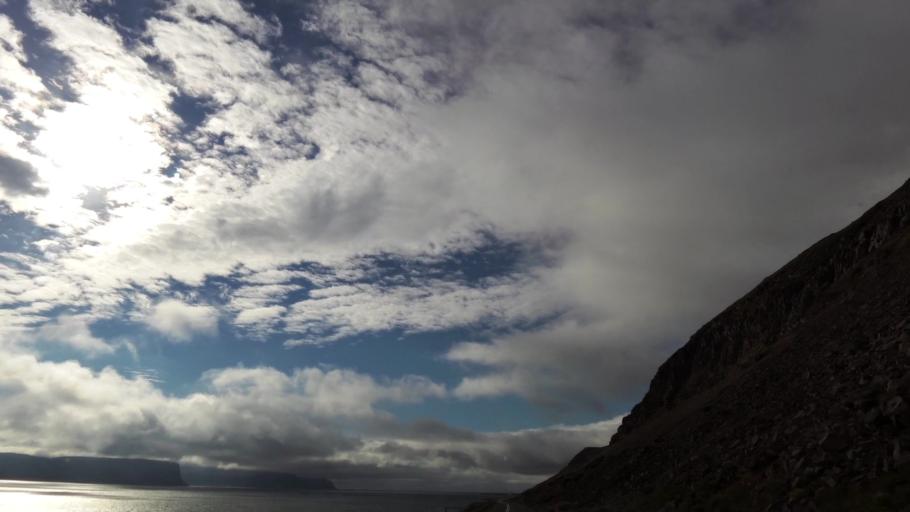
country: IS
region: West
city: Olafsvik
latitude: 65.5691
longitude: -23.9291
